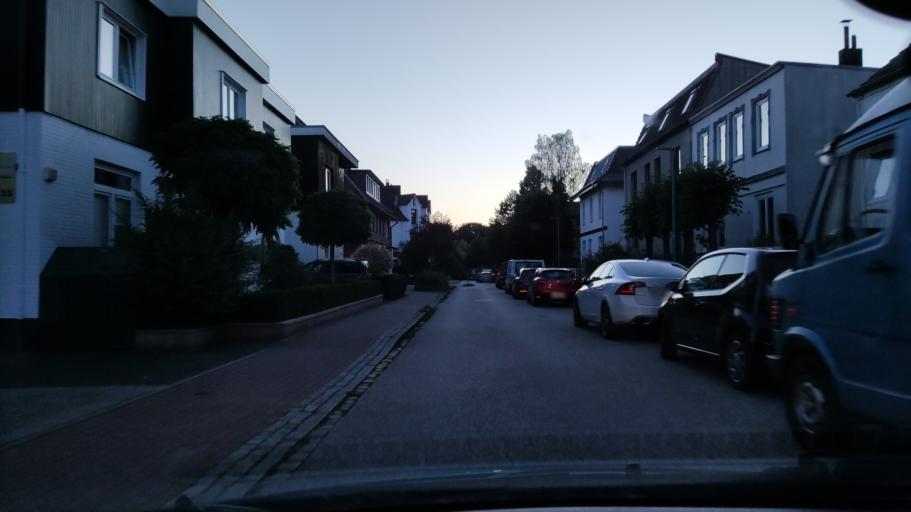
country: DE
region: Schleswig-Holstein
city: Wedel
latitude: 53.5713
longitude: 9.7126
